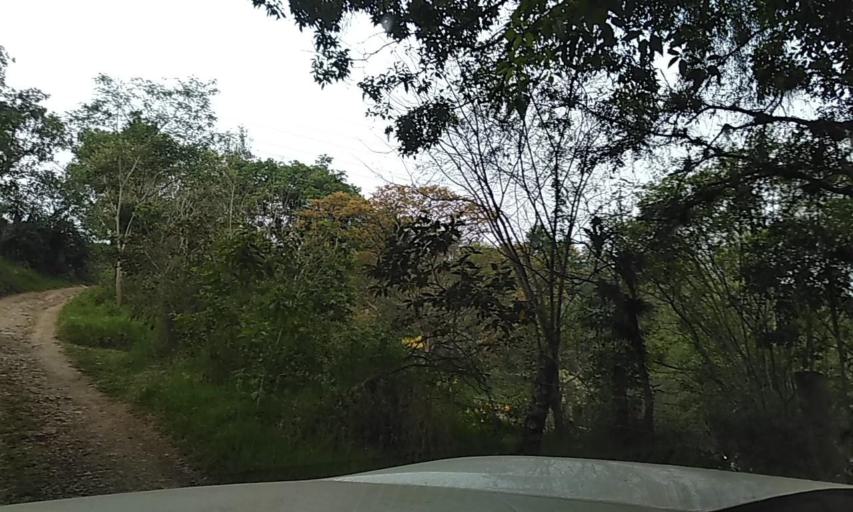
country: MX
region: Veracruz
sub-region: Xalapa
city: Lomas Verdes
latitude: 19.5018
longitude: -96.9162
